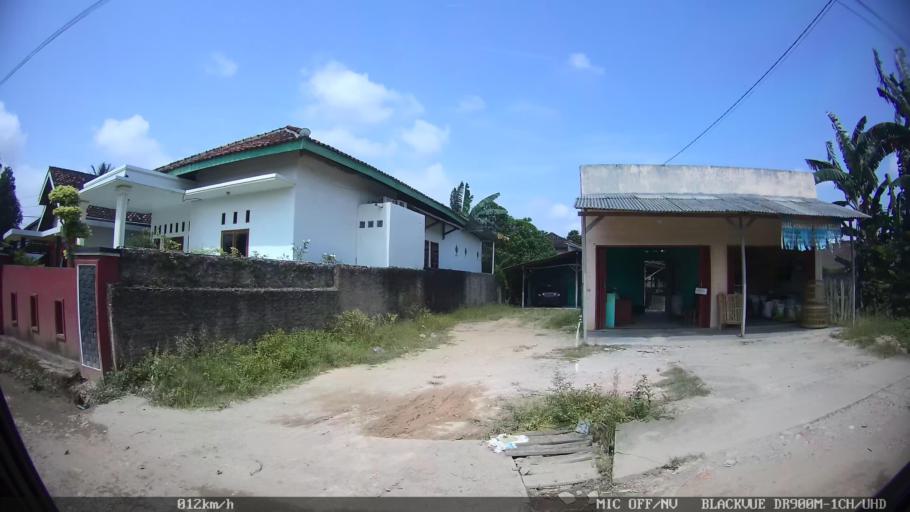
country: ID
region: Lampung
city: Kedaton
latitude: -5.3560
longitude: 105.2766
